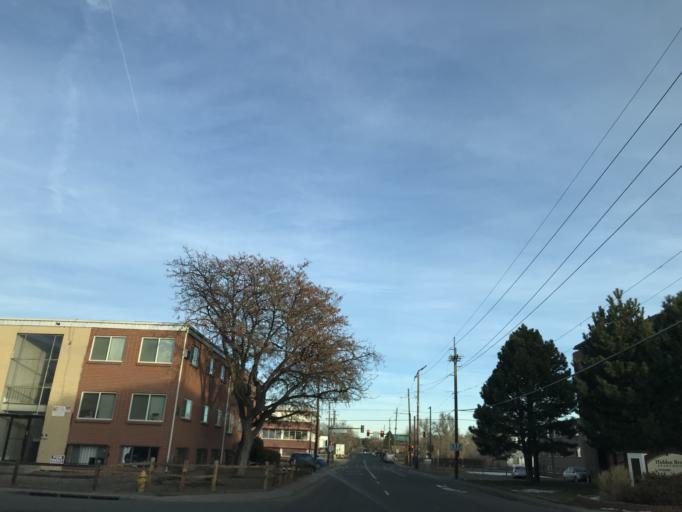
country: US
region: Colorado
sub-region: Adams County
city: Aurora
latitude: 39.7387
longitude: -104.8861
